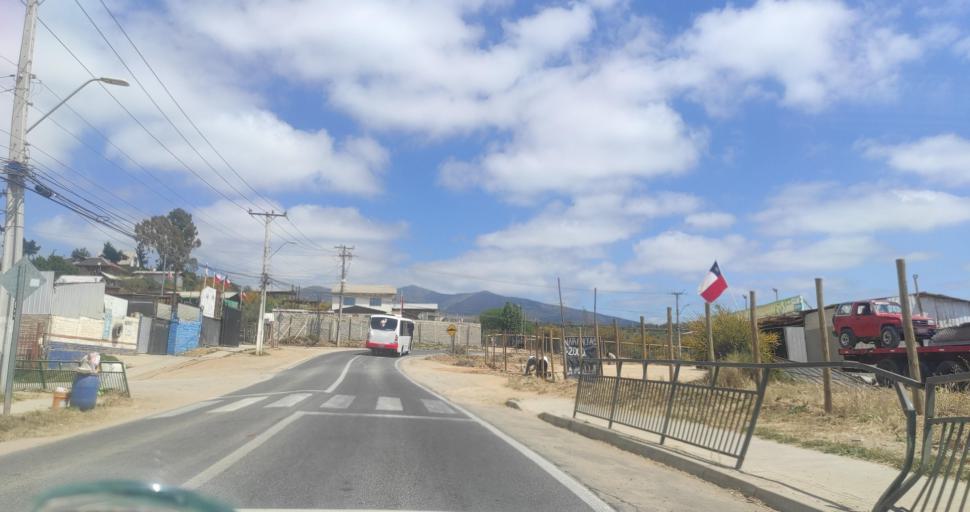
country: CL
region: Valparaiso
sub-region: Provincia de Marga Marga
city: Limache
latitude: -33.0220
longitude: -71.2559
